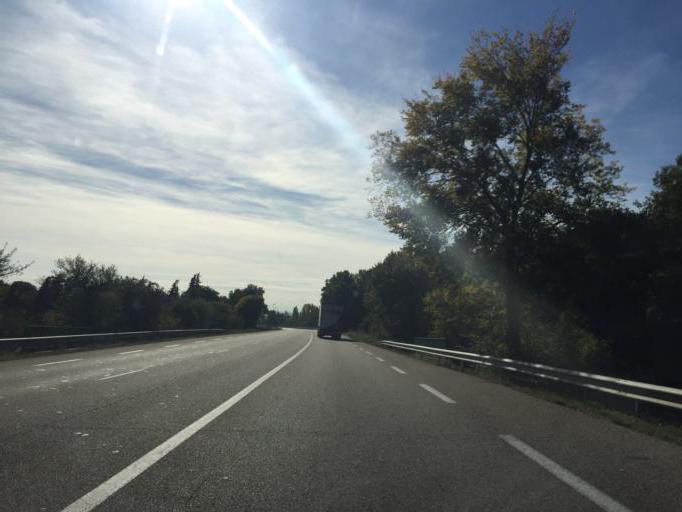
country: FR
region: Rhone-Alpes
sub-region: Departement de la Drome
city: Donzere
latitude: 44.4444
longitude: 4.7229
